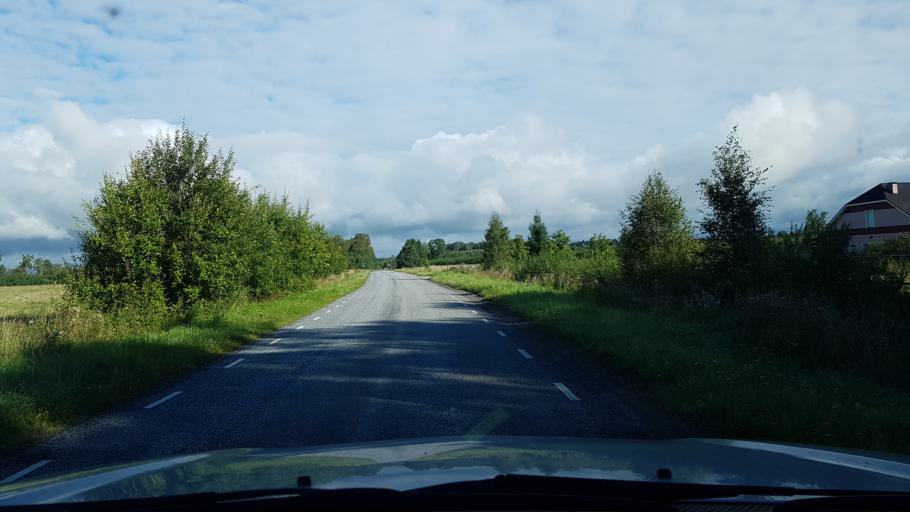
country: EE
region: Harju
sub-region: Rae vald
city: Vaida
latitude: 59.3046
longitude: 24.9270
